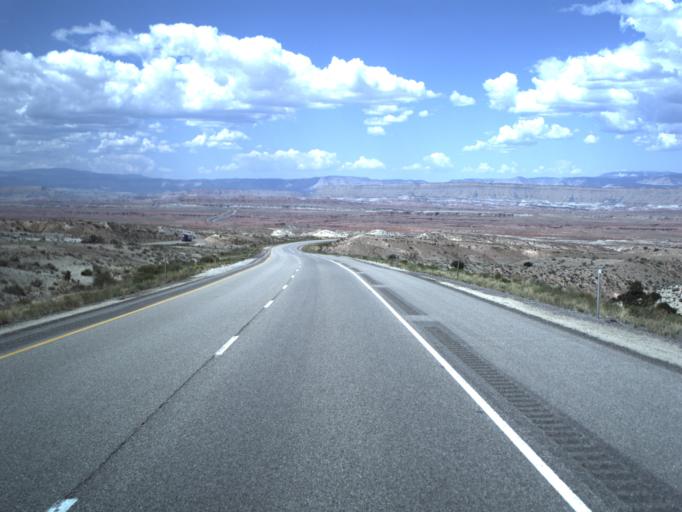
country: US
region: Utah
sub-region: Emery County
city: Ferron
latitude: 38.8441
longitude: -110.9755
